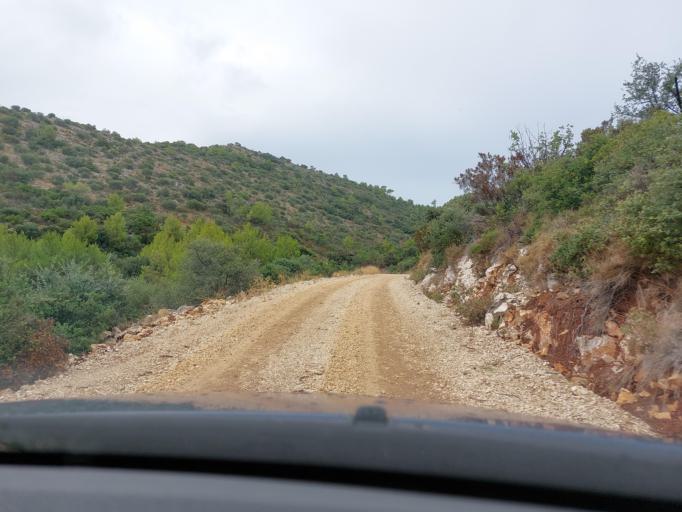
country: HR
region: Dubrovacko-Neretvanska
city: Smokvica
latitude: 42.7416
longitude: 16.9131
